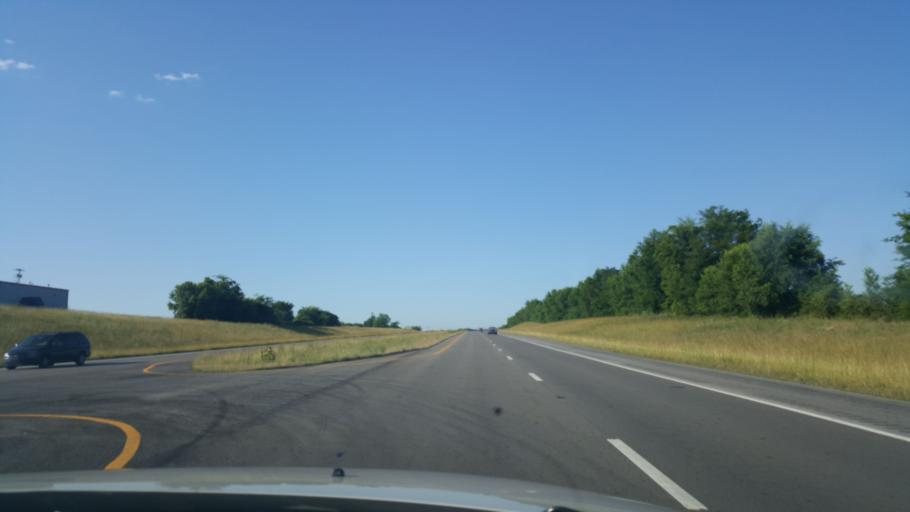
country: US
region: Tennessee
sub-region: Maury County
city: Columbia
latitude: 35.6074
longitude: -87.1216
